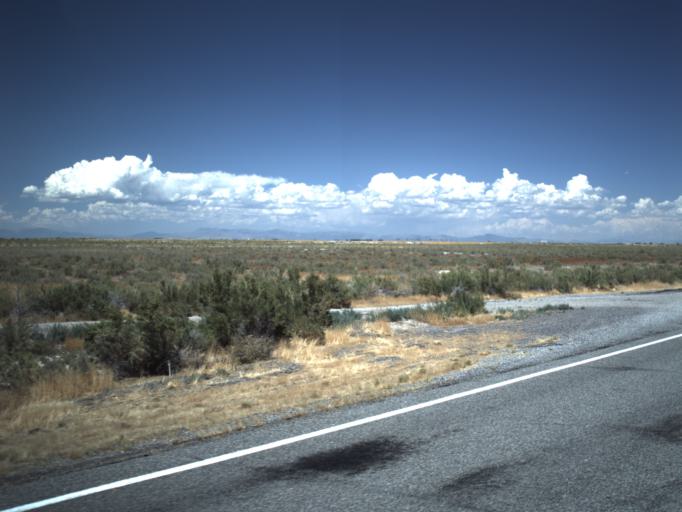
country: US
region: Utah
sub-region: Millard County
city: Delta
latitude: 39.3164
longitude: -112.7489
